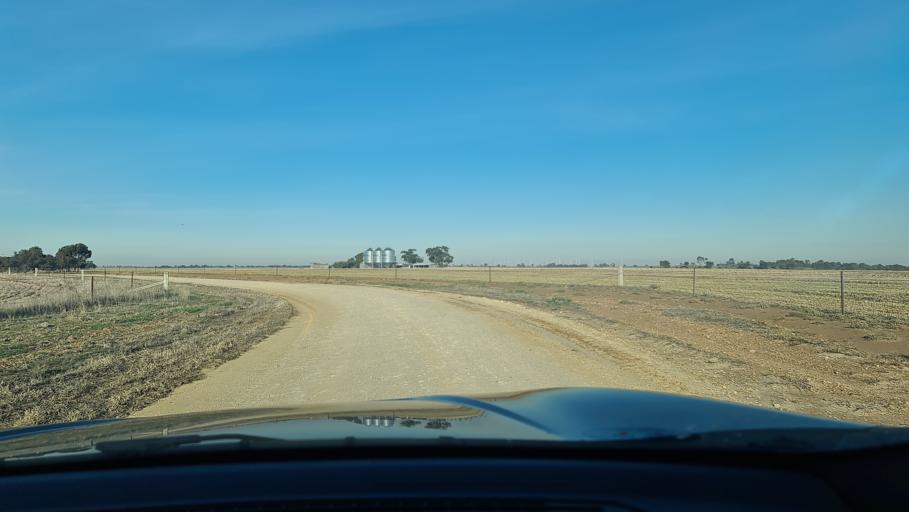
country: AU
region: Victoria
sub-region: Horsham
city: Horsham
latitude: -36.3616
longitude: 142.3960
